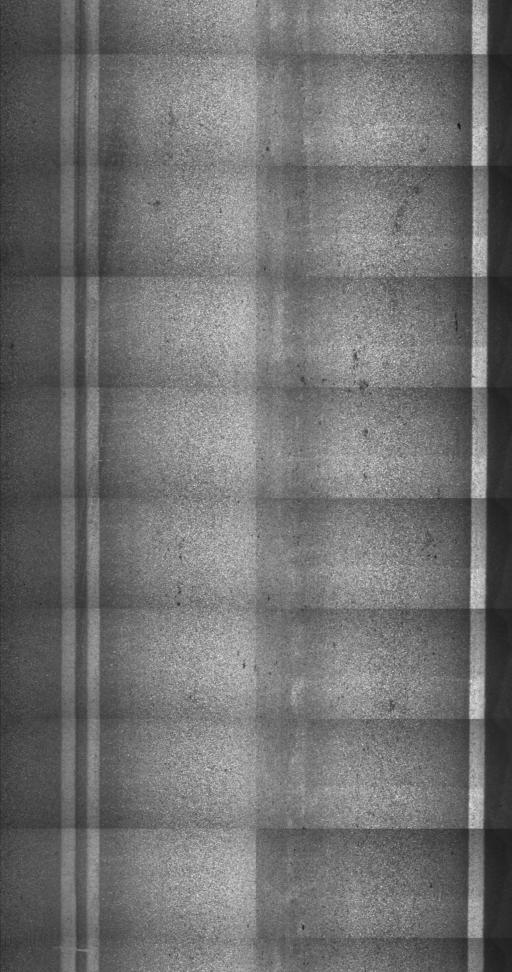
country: US
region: Vermont
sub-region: Windsor County
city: Springfield
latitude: 43.3665
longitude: -72.5180
